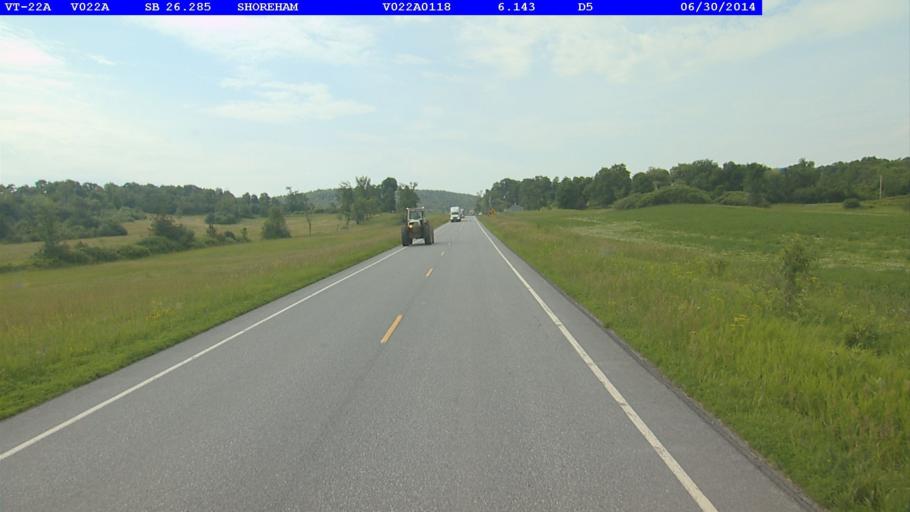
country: US
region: New York
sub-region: Essex County
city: Ticonderoga
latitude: 43.9373
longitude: -73.3105
